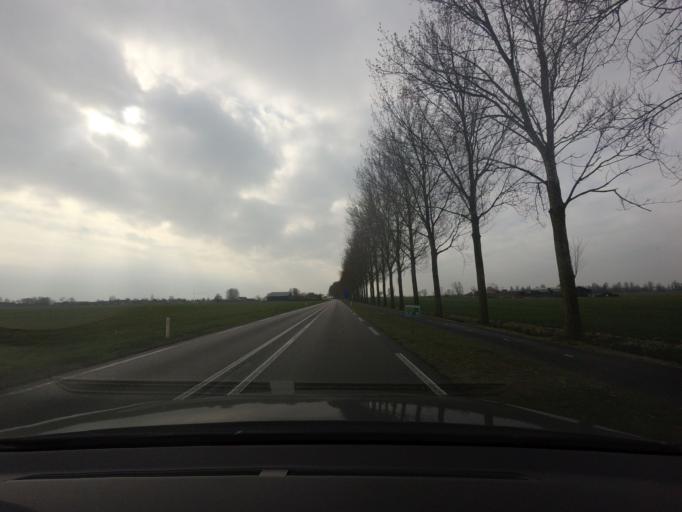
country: NL
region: Utrecht
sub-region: Gemeente De Ronde Venen
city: Mijdrecht
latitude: 52.1668
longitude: 4.9058
